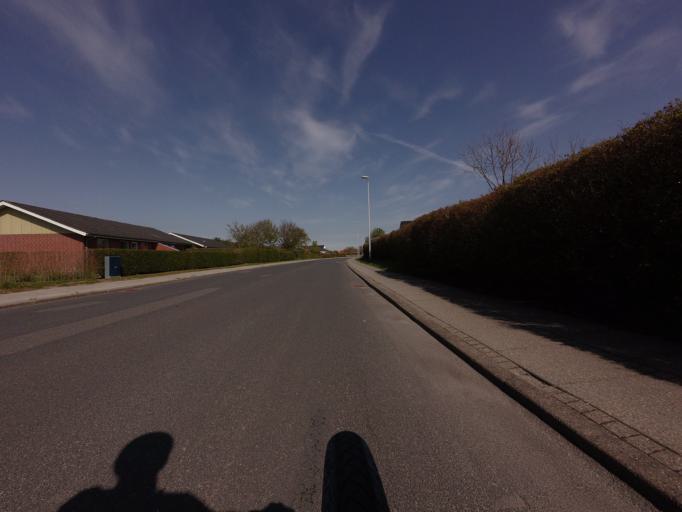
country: DK
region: North Denmark
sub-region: Jammerbugt Kommune
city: Pandrup
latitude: 57.2216
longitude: 9.6663
